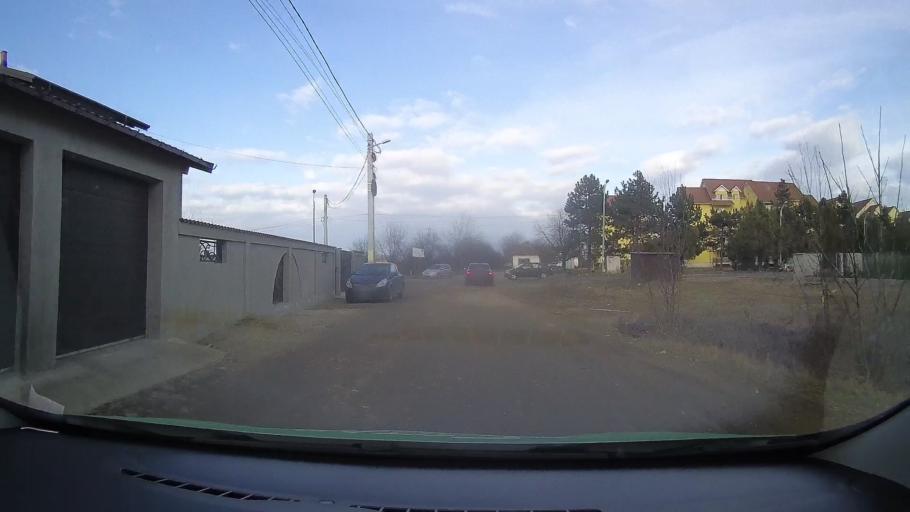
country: RO
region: Dambovita
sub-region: Comuna Ulmi
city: Ulmi
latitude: 44.9000
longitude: 25.5016
